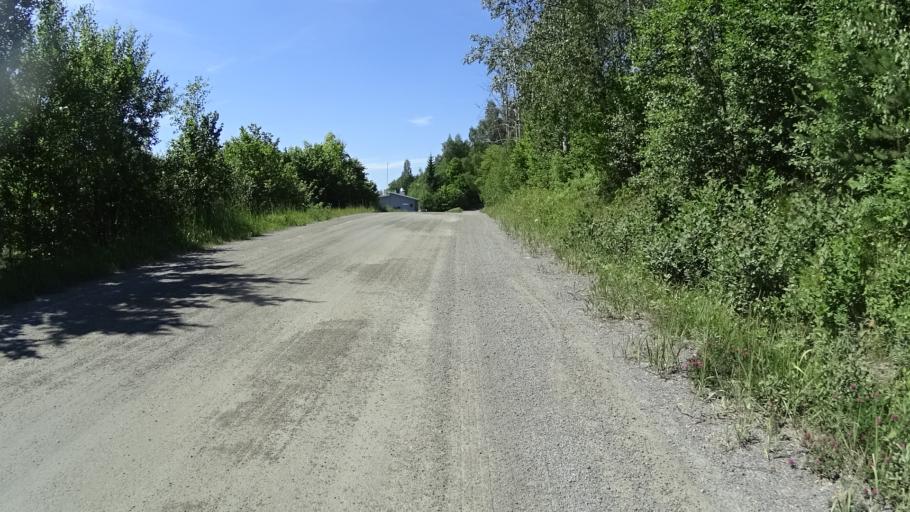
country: FI
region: Uusimaa
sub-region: Raaseporin
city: Pohja
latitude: 60.0947
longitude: 23.5693
